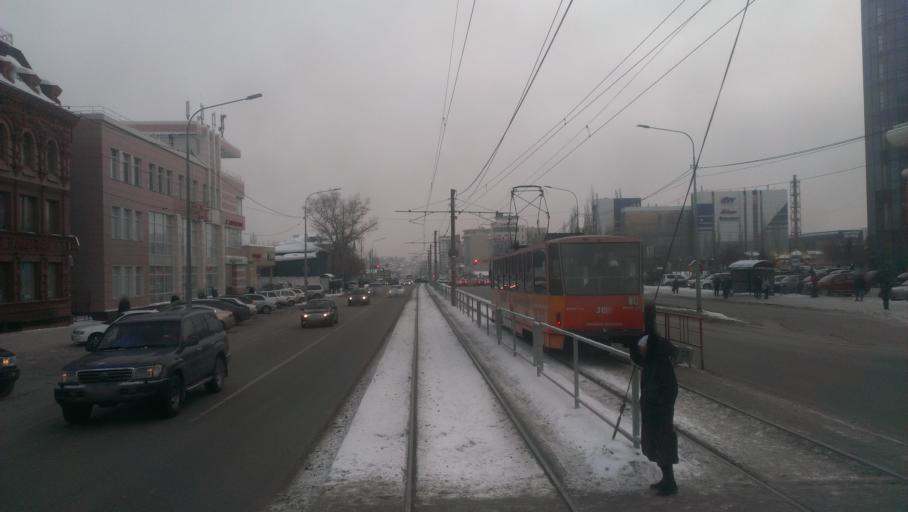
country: RU
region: Altai Krai
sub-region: Gorod Barnaulskiy
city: Barnaul
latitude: 53.3377
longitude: 83.7745
